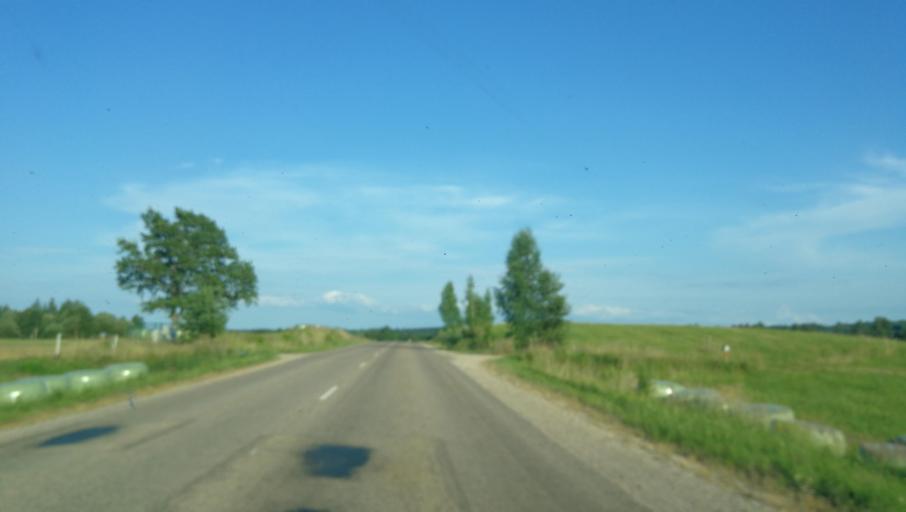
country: LV
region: Priekuli
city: Priekuli
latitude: 57.2704
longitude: 25.3400
